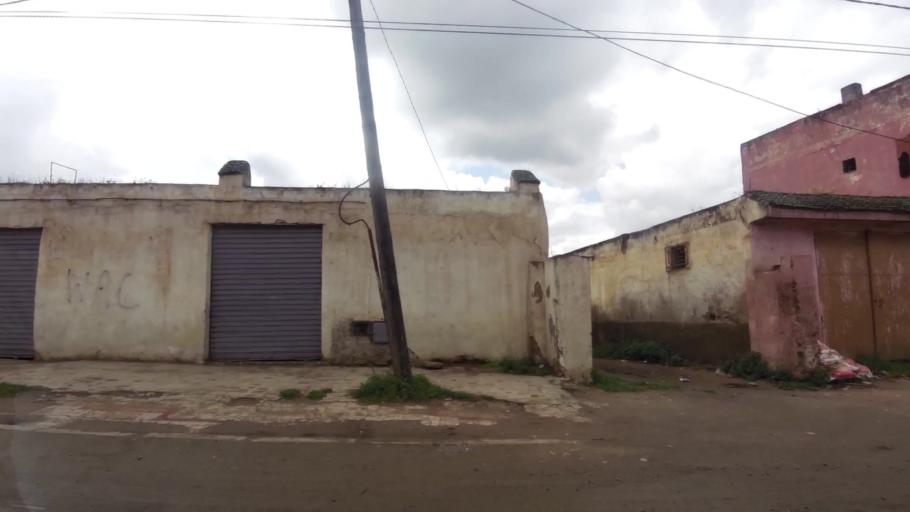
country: MA
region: Grand Casablanca
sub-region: Nouaceur
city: Bouskoura
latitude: 33.5155
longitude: -7.6393
